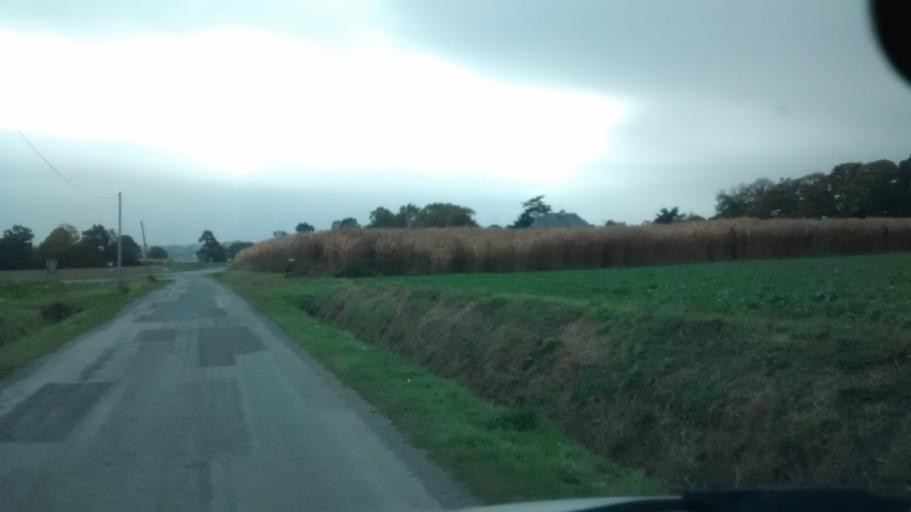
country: FR
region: Brittany
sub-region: Departement d'Ille-et-Vilaine
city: Noyal-sur-Vilaine
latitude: 48.1310
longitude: -1.5043
